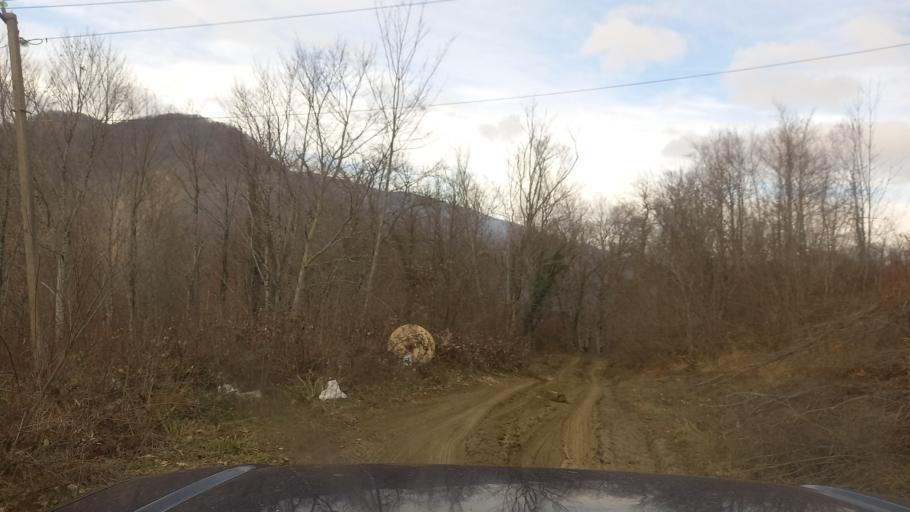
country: RU
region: Krasnodarskiy
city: Neftegorsk
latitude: 44.2031
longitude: 39.7043
